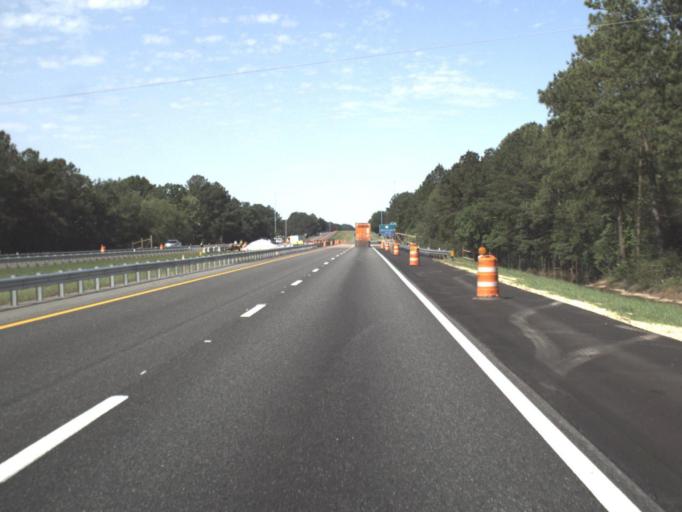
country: US
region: Florida
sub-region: Walton County
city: DeFuniak Springs
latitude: 30.7179
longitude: -85.9259
